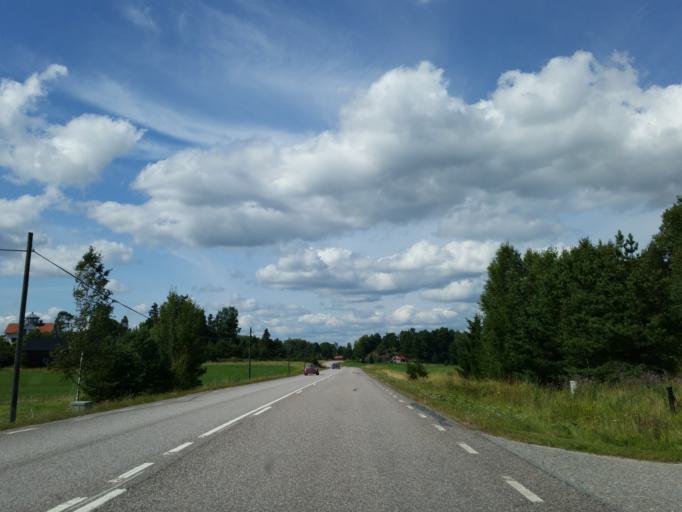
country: SE
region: Soedermanland
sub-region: Trosa Kommun
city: Vagnharad
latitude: 58.9964
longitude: 17.6108
